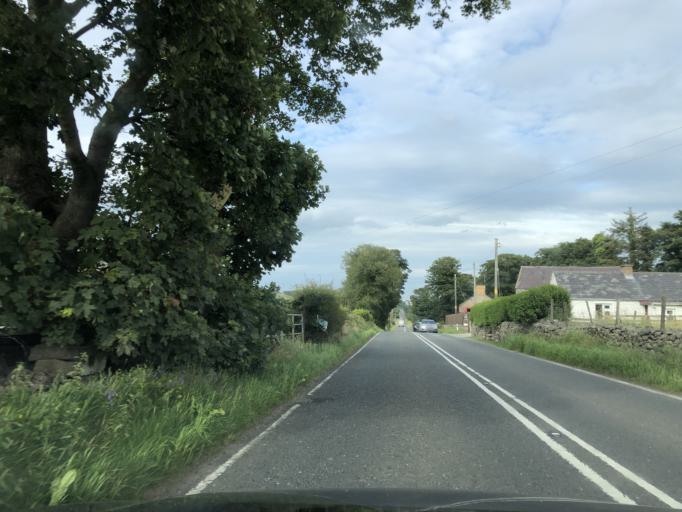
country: GB
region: Northern Ireland
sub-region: Down District
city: Castlewellan
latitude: 54.2412
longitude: -5.9925
